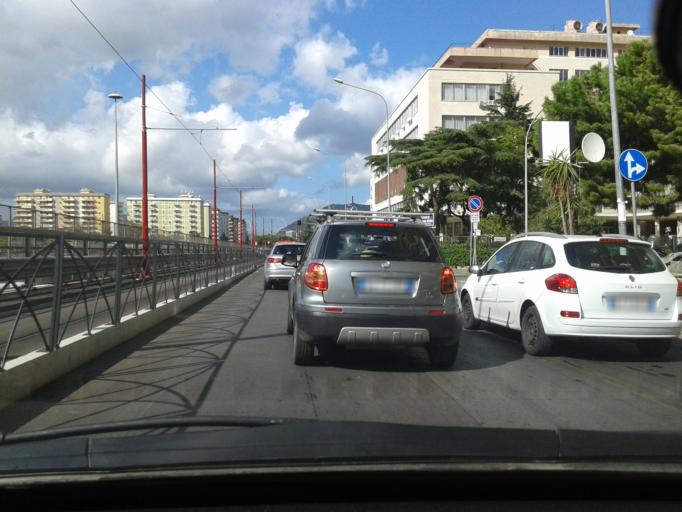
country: IT
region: Sicily
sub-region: Palermo
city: Palermo
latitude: 38.1274
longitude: 13.3299
